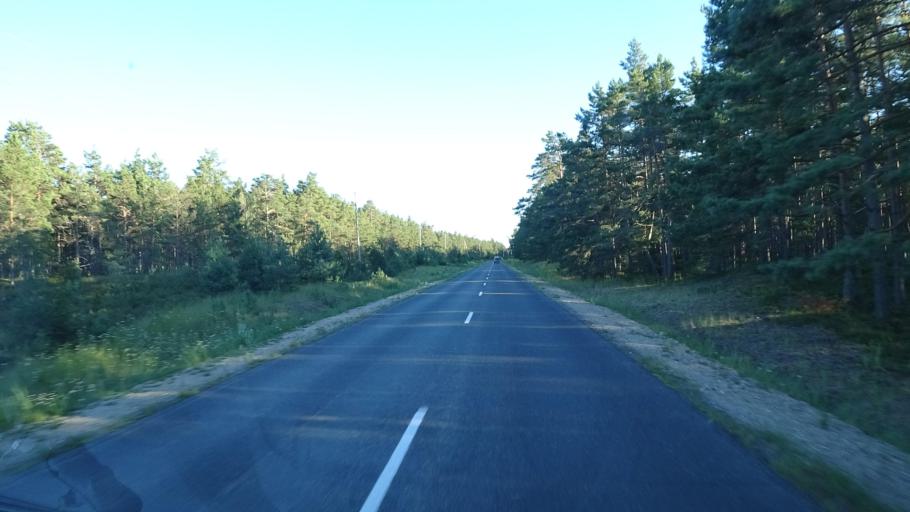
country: LV
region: Dundaga
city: Dundaga
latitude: 57.7165
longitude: 22.5719
